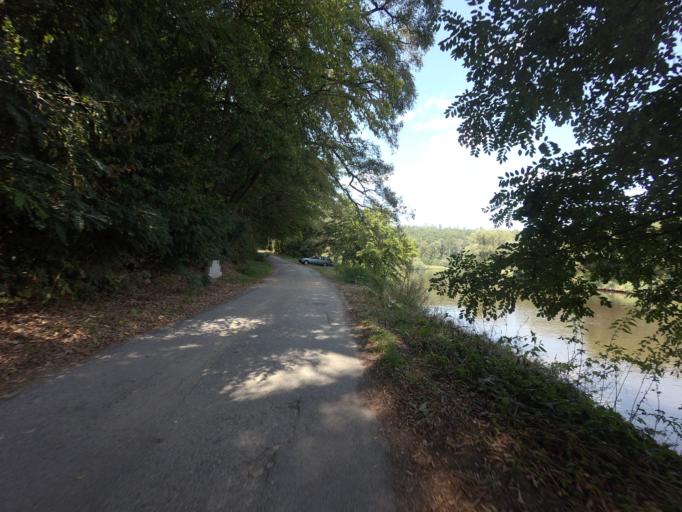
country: CZ
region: Jihocesky
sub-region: Okres Ceske Budejovice
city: Hluboka nad Vltavou
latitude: 49.0602
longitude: 14.4430
